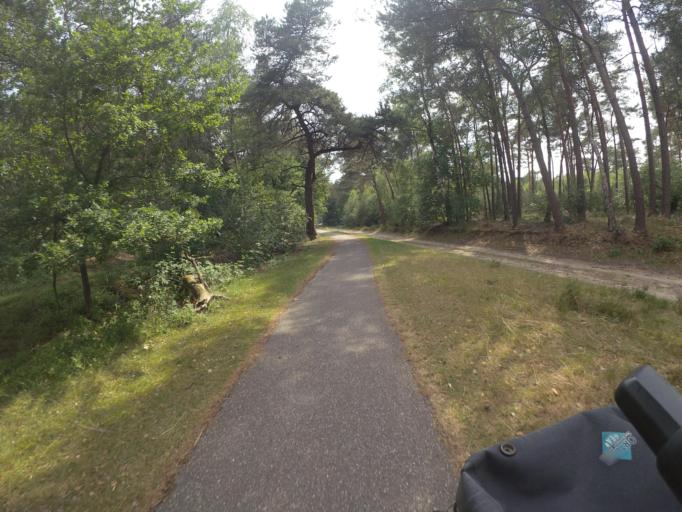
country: NL
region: Overijssel
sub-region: Gemeente Twenterand
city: Den Ham
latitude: 52.4738
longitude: 6.3973
